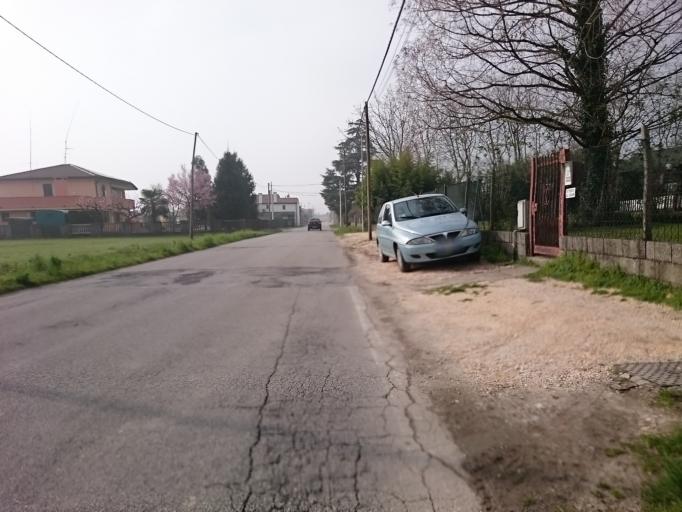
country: IT
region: Veneto
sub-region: Provincia di Padova
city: Bertipaglia
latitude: 45.3192
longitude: 11.8848
